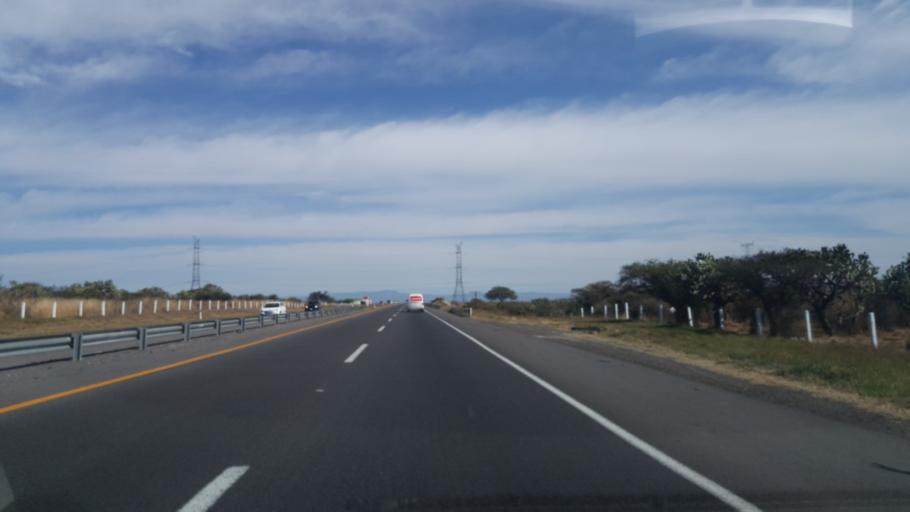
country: MX
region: Jalisco
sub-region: Lagos de Moreno
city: Cristeros [Fraccionamiento]
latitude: 21.3074
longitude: -102.0796
